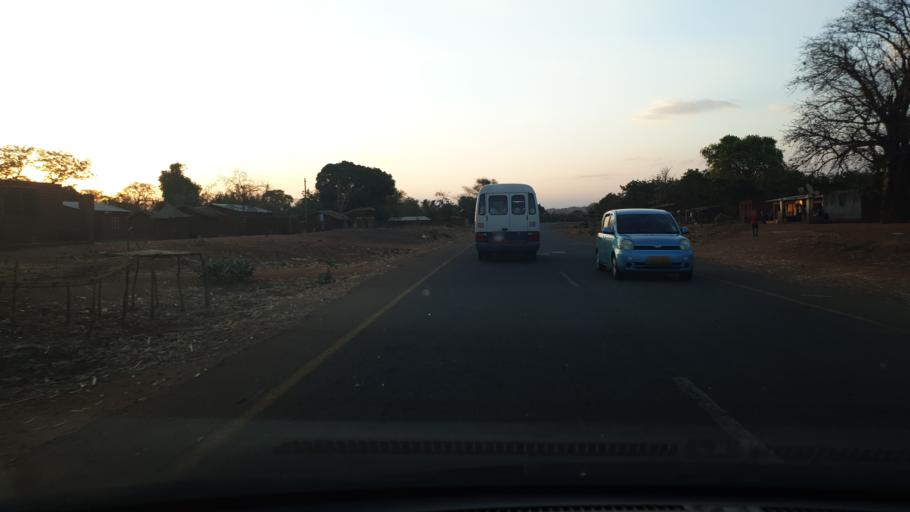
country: MW
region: Central Region
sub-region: Salima District
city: Salima
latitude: -13.7646
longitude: 34.3450
